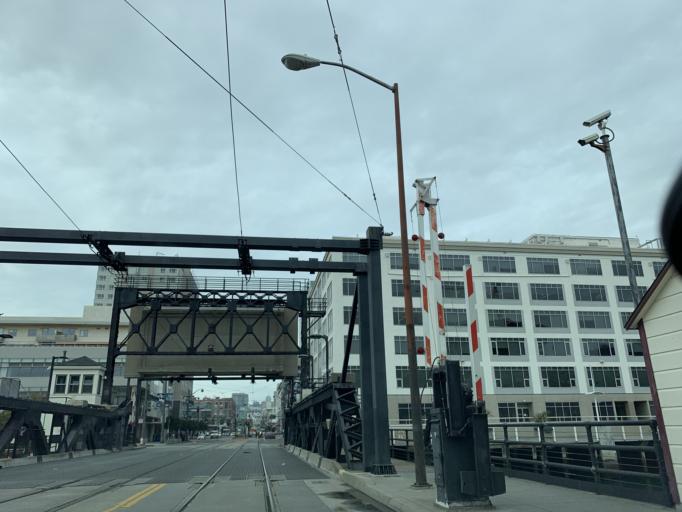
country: US
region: California
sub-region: San Francisco County
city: San Francisco
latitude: 37.7749
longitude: -122.3922
